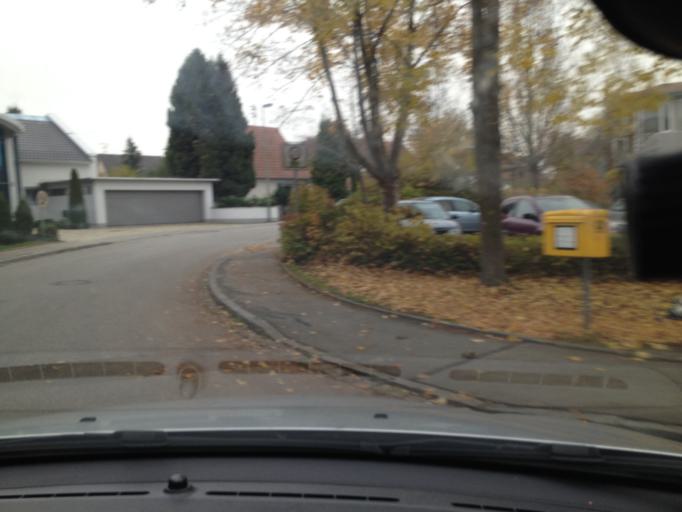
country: DE
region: Bavaria
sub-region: Swabia
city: Langerringen
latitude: 48.1512
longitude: 10.7548
